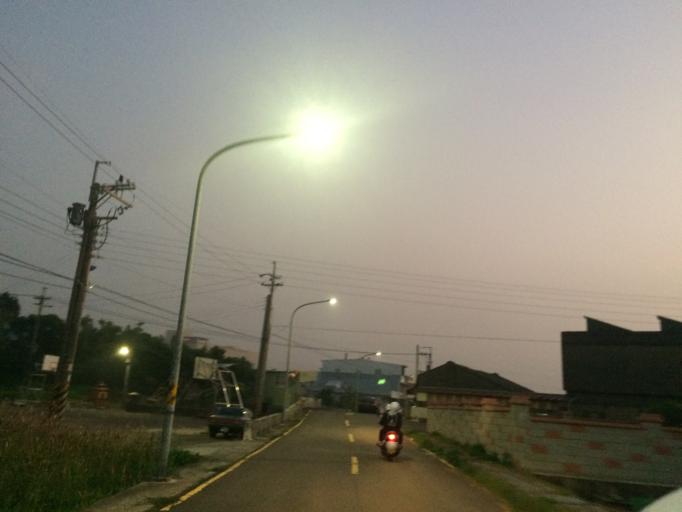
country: TW
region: Taiwan
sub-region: Hsinchu
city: Hsinchu
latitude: 24.7730
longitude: 120.9154
